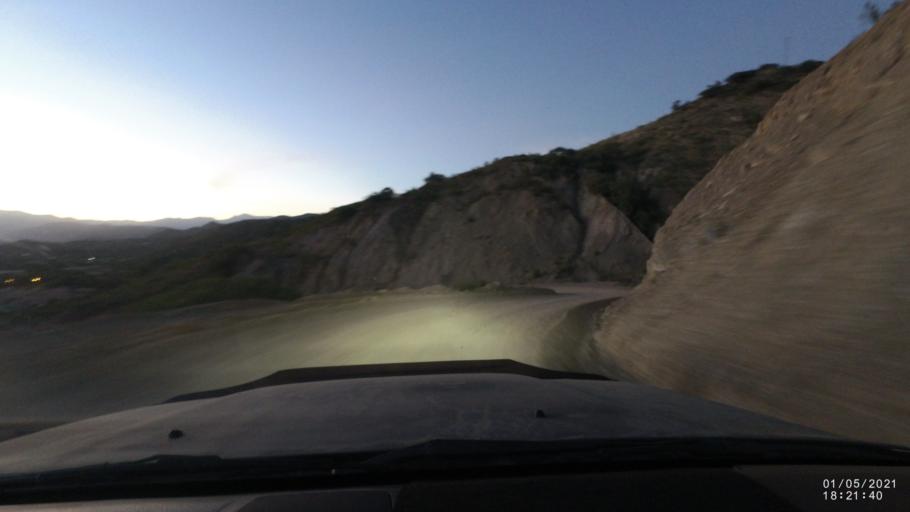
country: BO
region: Cochabamba
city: Capinota
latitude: -17.6616
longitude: -66.2307
